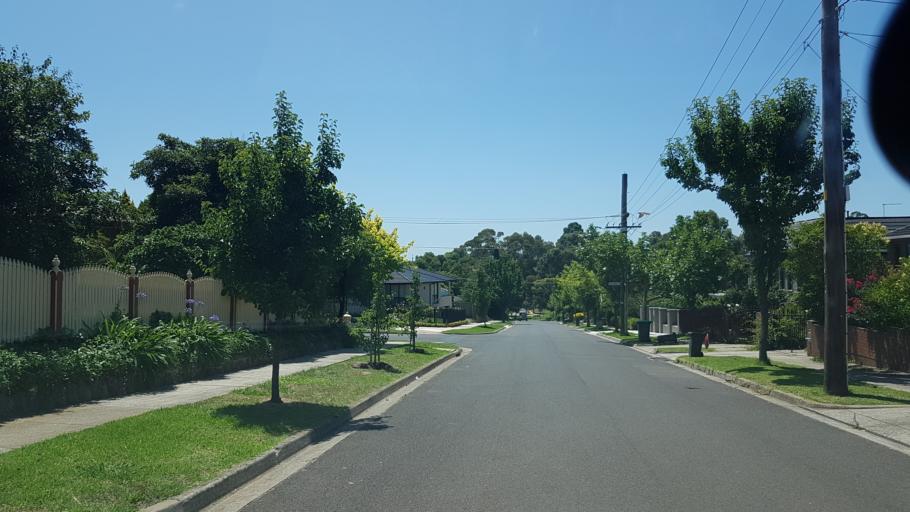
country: AU
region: Victoria
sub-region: Manningham
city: Bulleen
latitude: -37.7642
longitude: 145.0990
